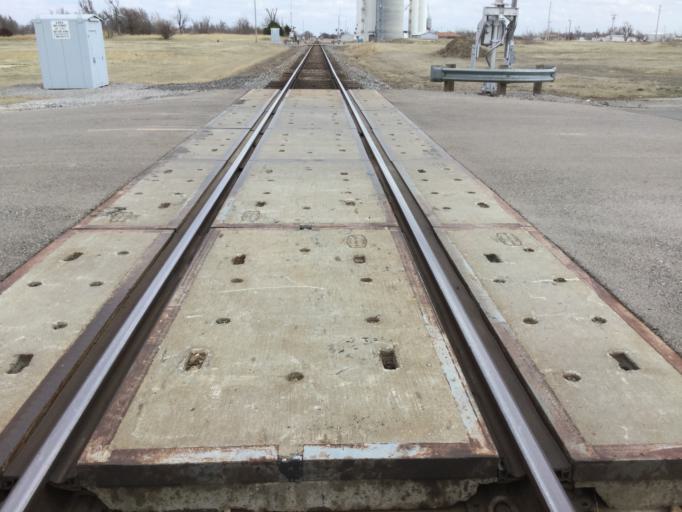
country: US
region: Kansas
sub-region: Kiowa County
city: Greensburg
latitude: 37.6093
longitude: -99.2983
